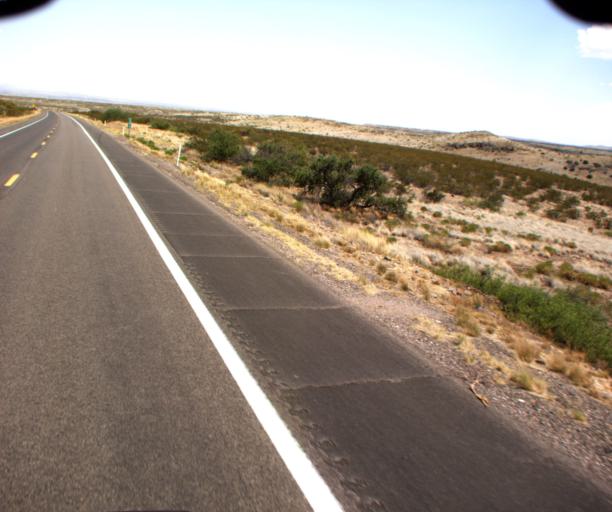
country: US
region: Arizona
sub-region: Greenlee County
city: Clifton
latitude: 32.7304
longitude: -109.1861
